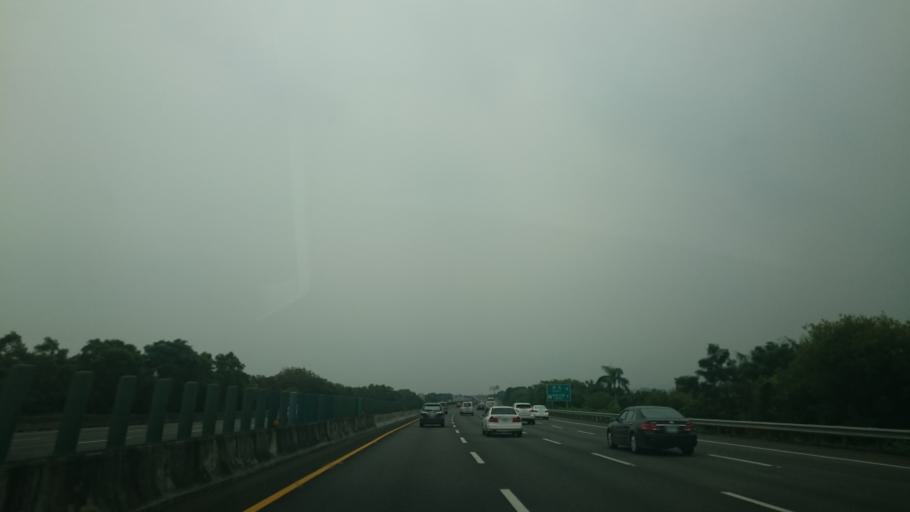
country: TW
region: Taiwan
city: Zhongxing New Village
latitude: 23.9734
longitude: 120.6492
